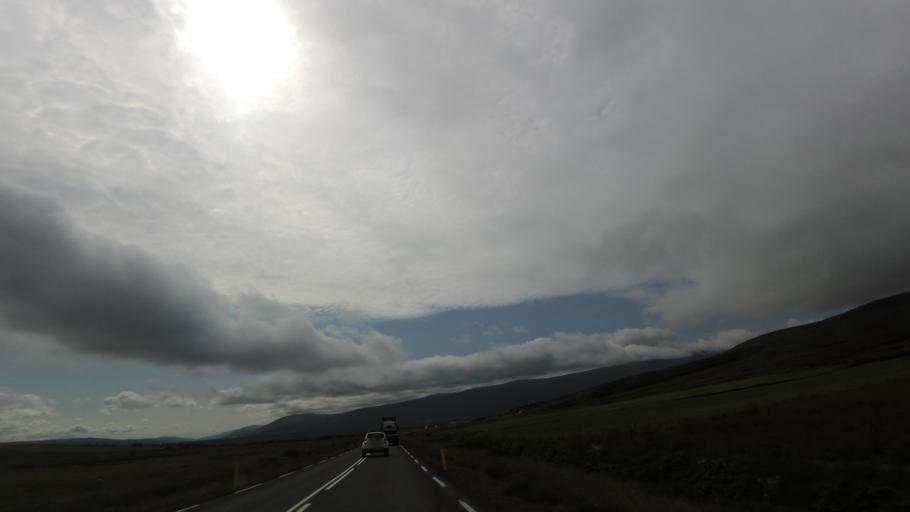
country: IS
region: Northeast
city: Laugar
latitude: 65.7334
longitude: -17.5909
